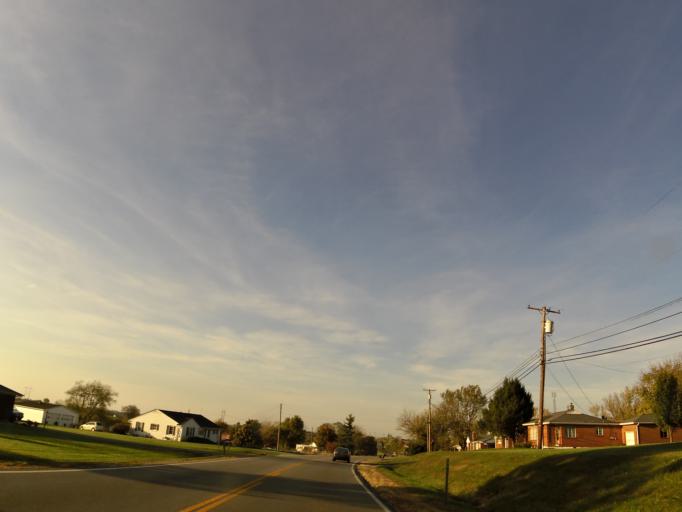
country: US
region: Kentucky
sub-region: Garrard County
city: Lancaster
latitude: 37.6302
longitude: -84.5803
